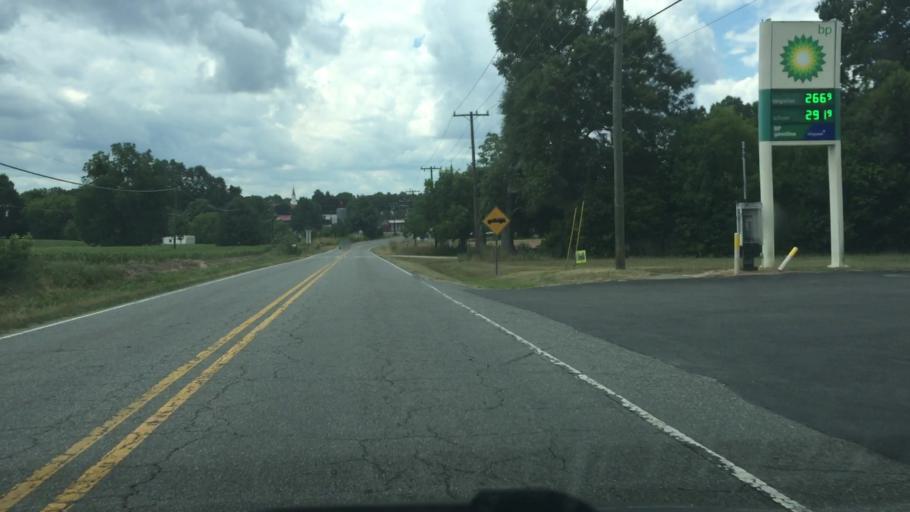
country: US
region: North Carolina
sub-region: Rowan County
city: Enochville
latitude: 35.5339
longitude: -80.6658
